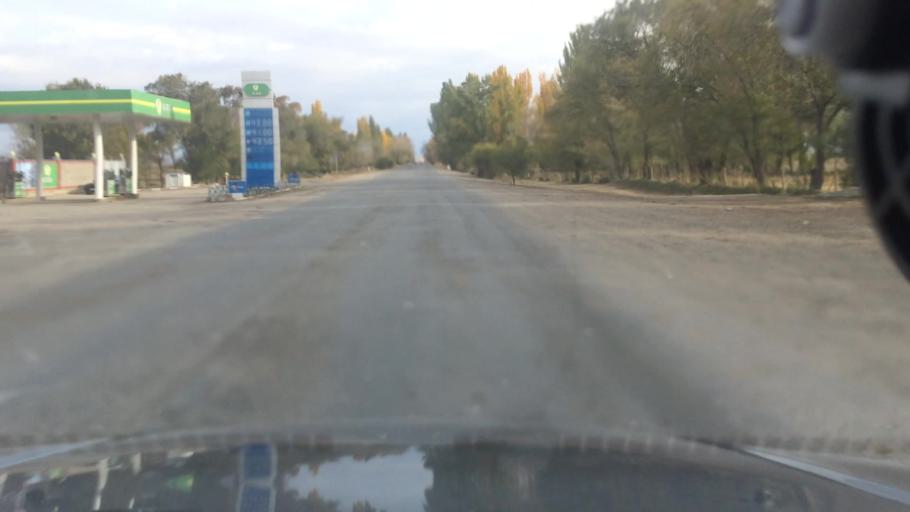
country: KG
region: Ysyk-Koel
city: Karakol
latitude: 42.5394
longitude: 78.3835
